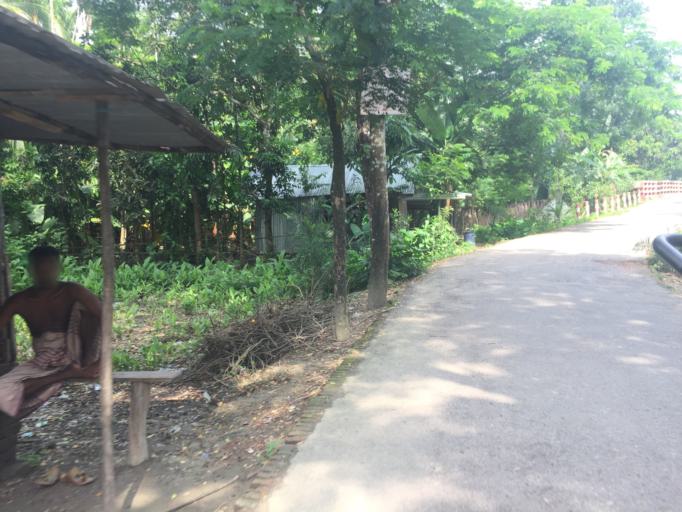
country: BD
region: Barisal
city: Mathba
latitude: 22.2613
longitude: 89.9115
